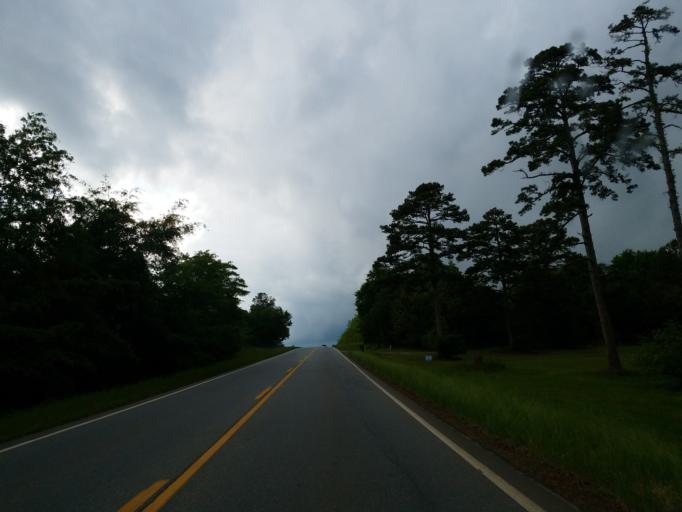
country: US
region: Georgia
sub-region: Dooly County
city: Unadilla
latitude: 32.3380
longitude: -83.7722
